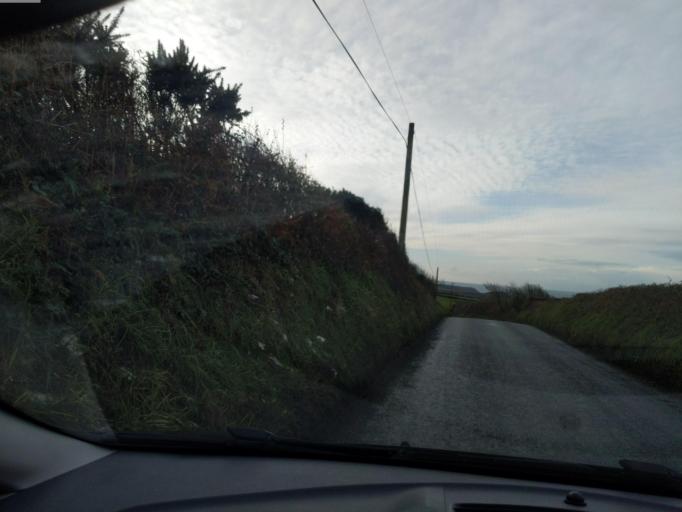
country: GB
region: England
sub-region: Cornwall
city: Camelford
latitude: 50.6970
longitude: -4.6650
